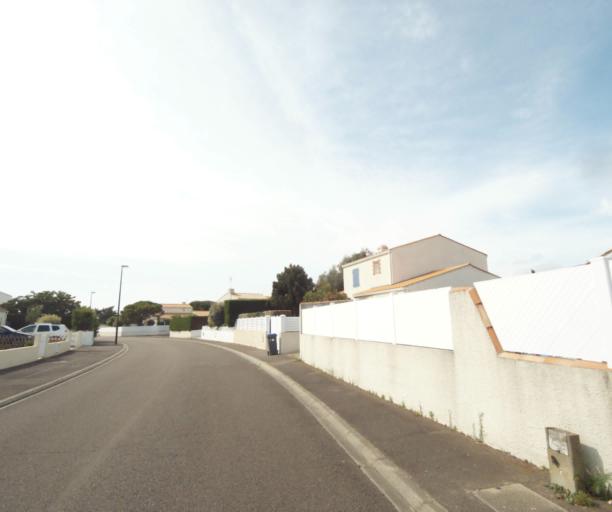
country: FR
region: Pays de la Loire
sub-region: Departement de la Vendee
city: Chateau-d'Olonne
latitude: 46.4810
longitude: -1.7513
